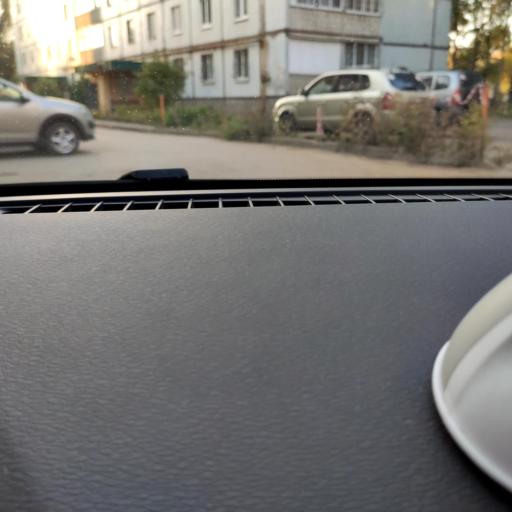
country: RU
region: Samara
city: Samara
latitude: 53.2422
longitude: 50.2462
